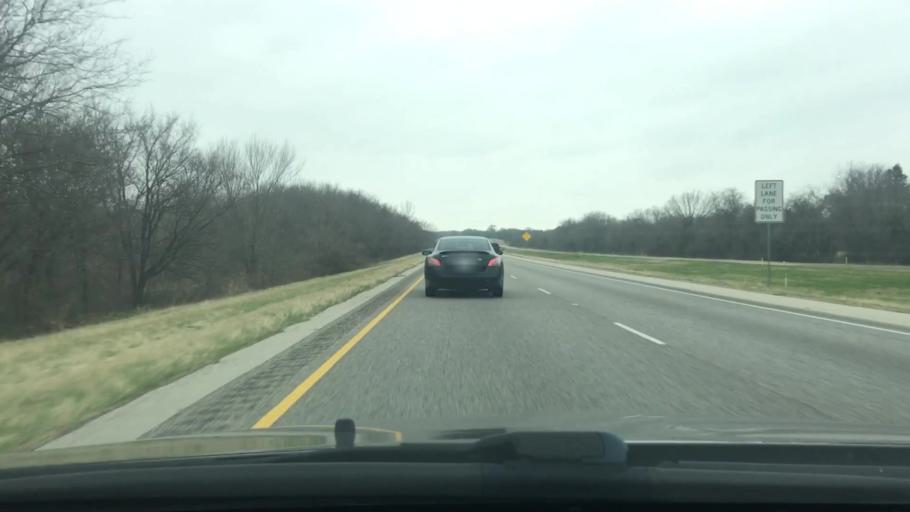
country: US
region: Texas
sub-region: Freestone County
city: Fairfield
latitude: 31.8002
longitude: -96.2583
